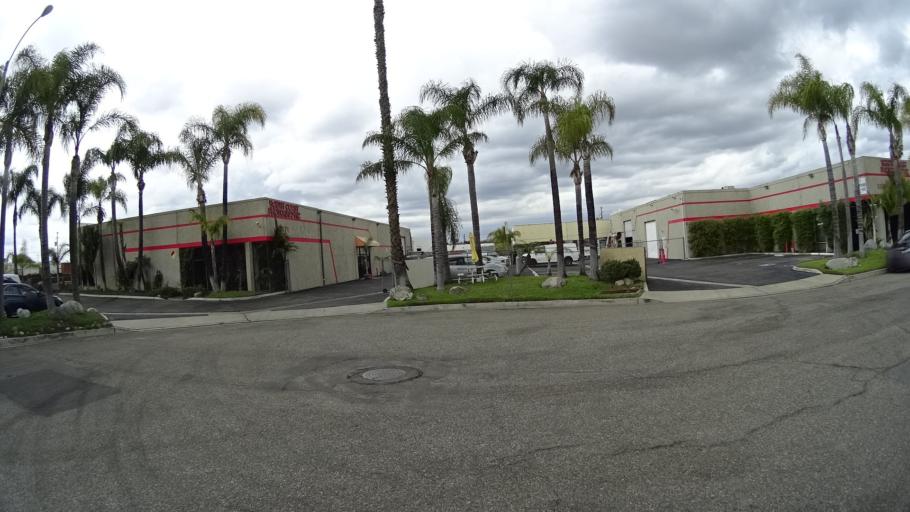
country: US
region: California
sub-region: Orange County
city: Placentia
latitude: 33.8603
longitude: -117.8617
